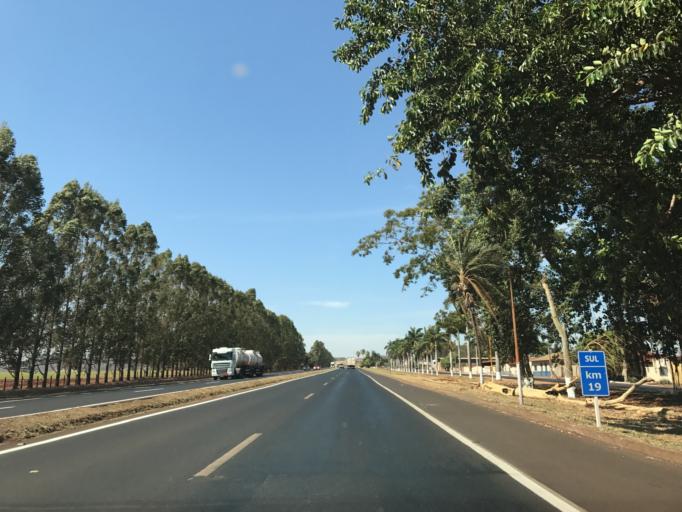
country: BR
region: Minas Gerais
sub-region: Centralina
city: Centralina
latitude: -18.5861
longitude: -49.1931
